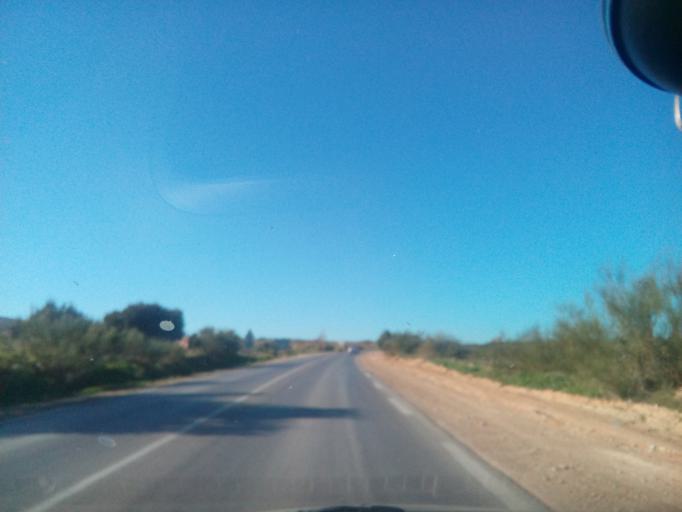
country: DZ
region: Relizane
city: Relizane
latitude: 35.9051
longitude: 0.5141
